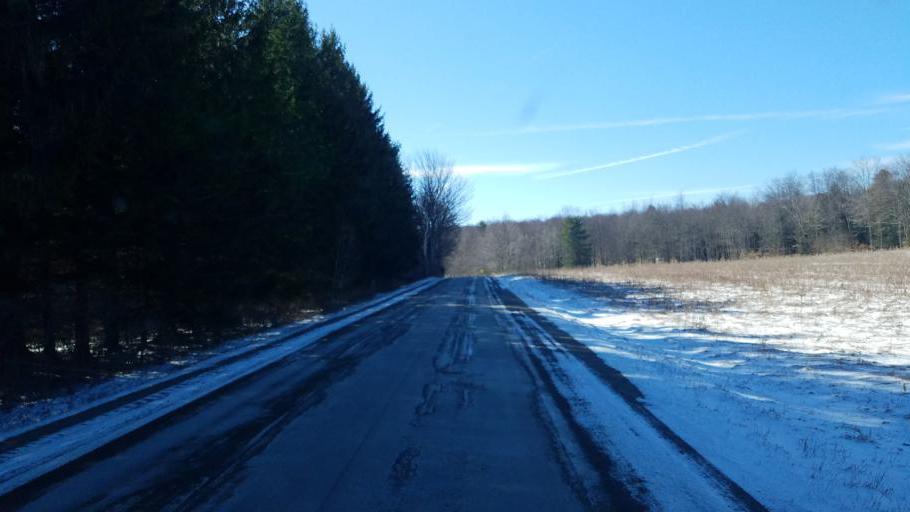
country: US
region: New York
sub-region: Allegany County
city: Wellsville
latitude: 42.0554
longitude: -78.0092
